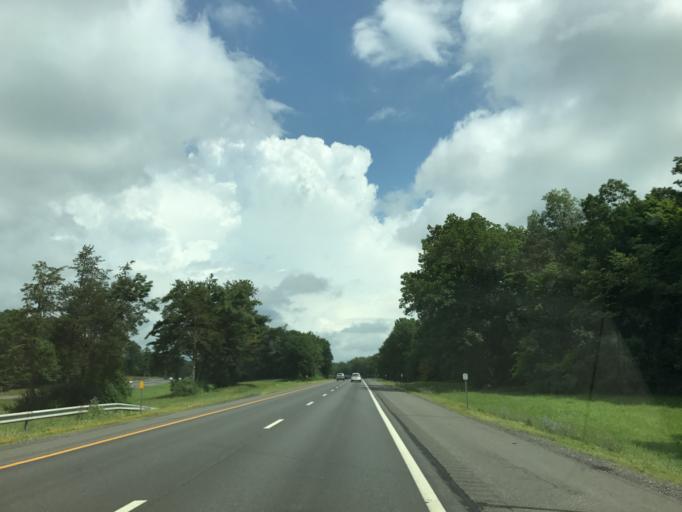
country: US
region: New York
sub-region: Greene County
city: Coxsackie
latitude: 42.3317
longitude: -73.8607
